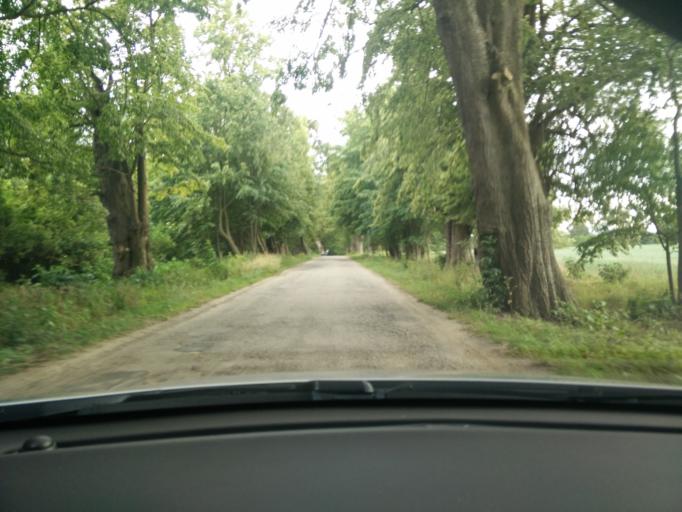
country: PL
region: Pomeranian Voivodeship
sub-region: Powiat pucki
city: Mrzezino
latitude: 54.6821
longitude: 18.4611
